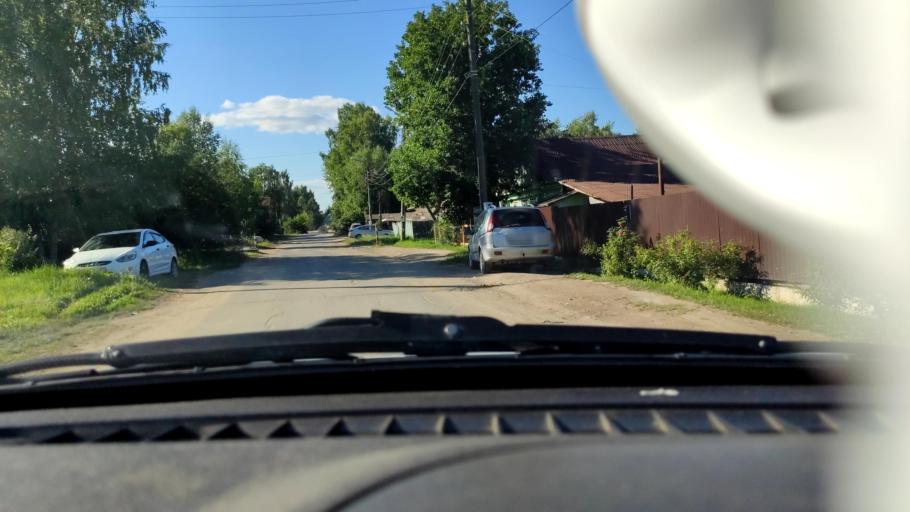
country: RU
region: Perm
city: Overyata
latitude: 58.0776
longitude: 55.8118
